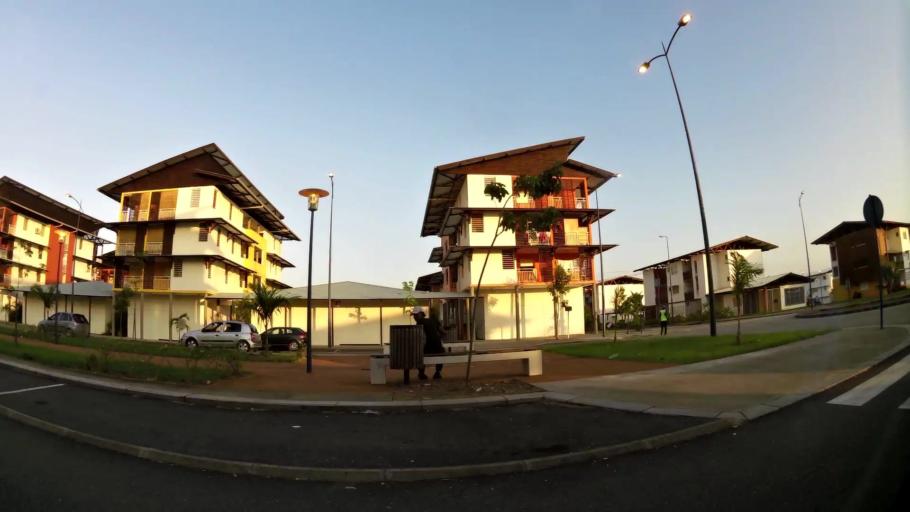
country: GF
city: Macouria
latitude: 4.9309
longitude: -52.4092
